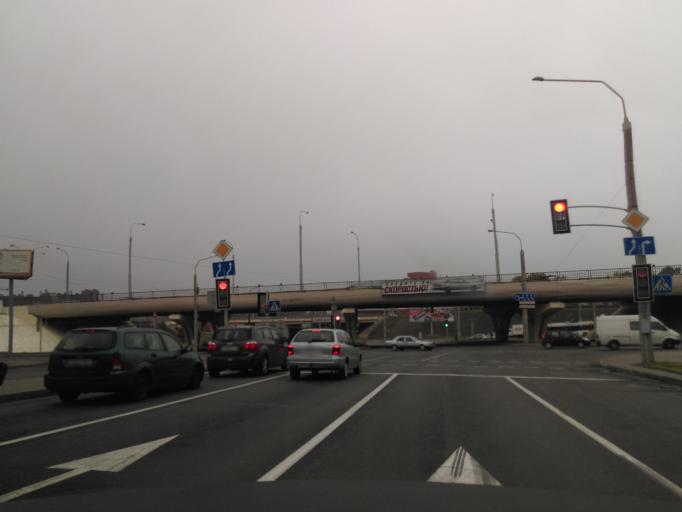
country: BY
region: Minsk
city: Minsk
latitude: 53.8864
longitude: 27.5799
